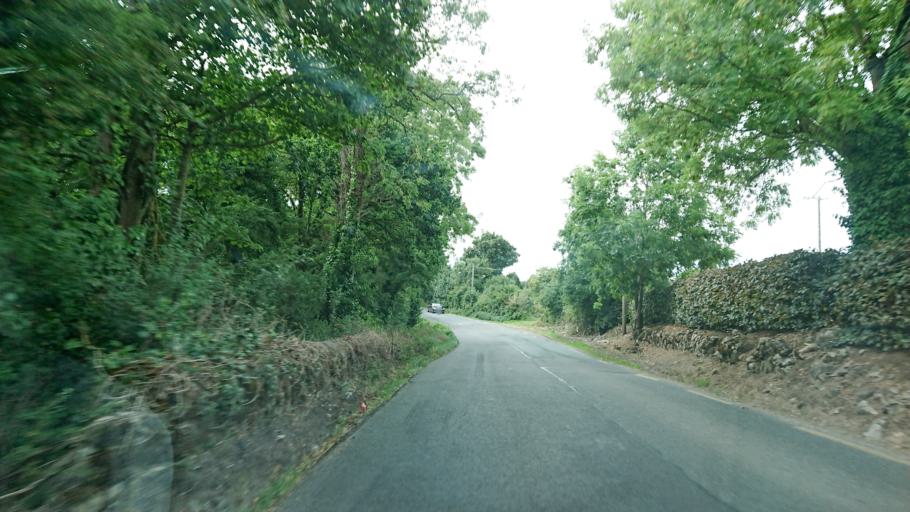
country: IE
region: Munster
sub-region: County Cork
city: Mallow
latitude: 52.1524
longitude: -8.5334
